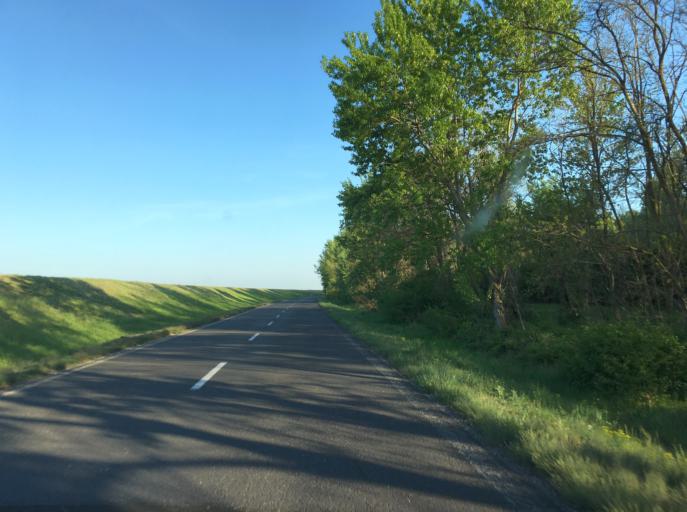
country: HU
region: Gyor-Moson-Sopron
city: Rajka
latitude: 48.0284
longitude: 17.2403
